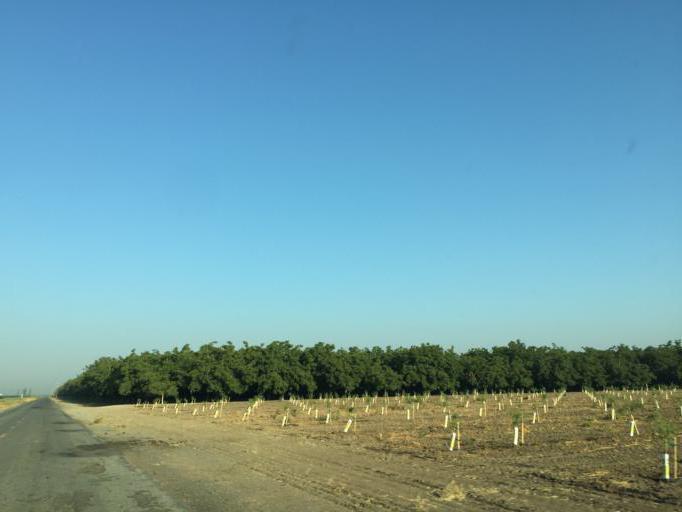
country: US
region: California
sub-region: Tulare County
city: London
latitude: 36.4586
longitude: -119.4067
